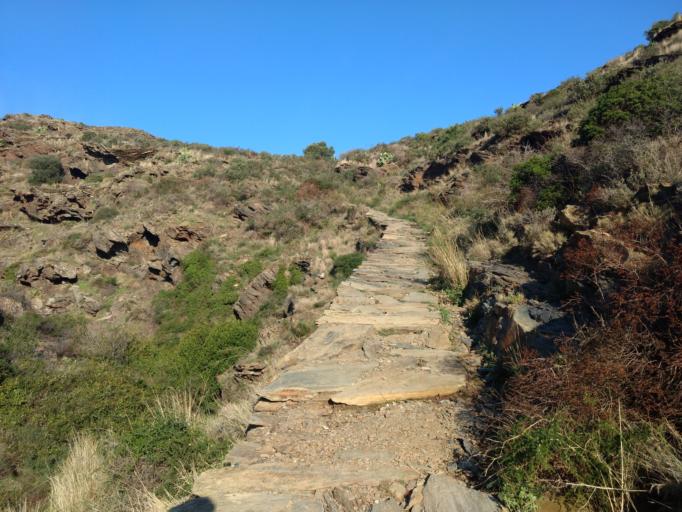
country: ES
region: Catalonia
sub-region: Provincia de Girona
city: Cadaques
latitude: 42.2713
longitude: 3.2813
